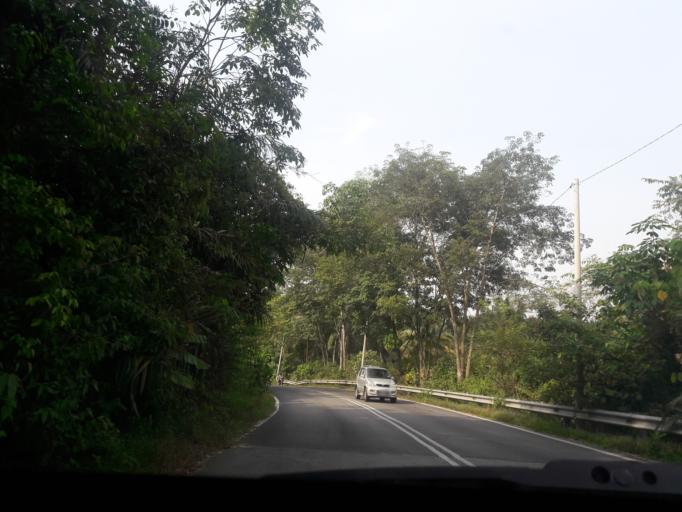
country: MY
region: Kedah
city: Kulim
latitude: 5.3684
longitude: 100.5223
